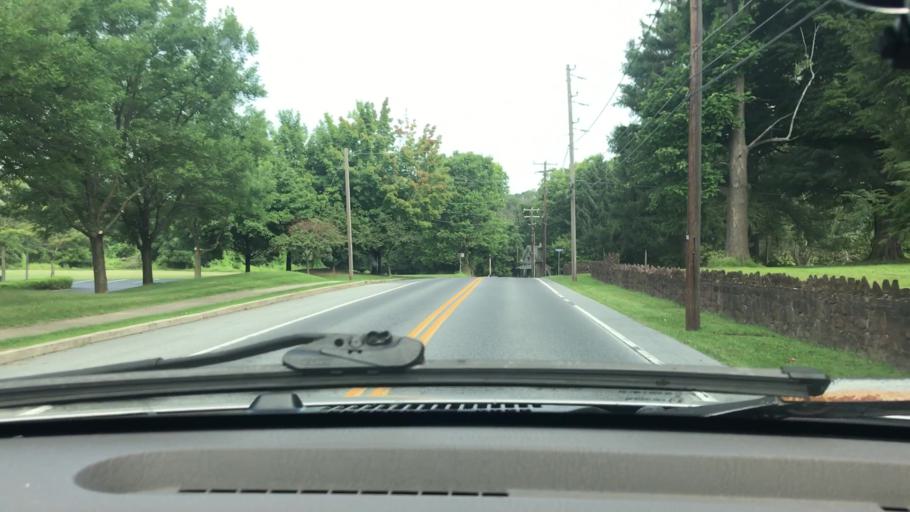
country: US
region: Pennsylvania
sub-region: Dauphin County
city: Middletown
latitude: 40.2066
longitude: -76.7608
